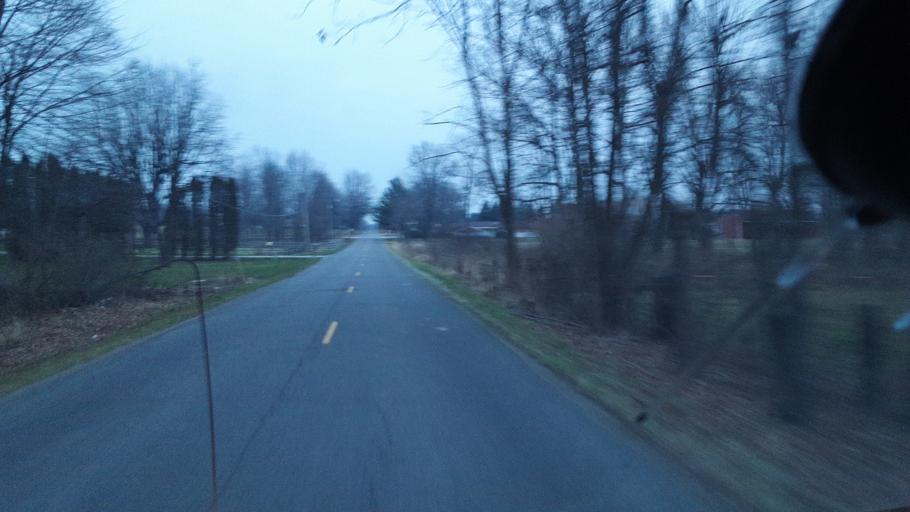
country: US
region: Indiana
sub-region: Elkhart County
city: Bristol
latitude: 41.6655
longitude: -85.7873
